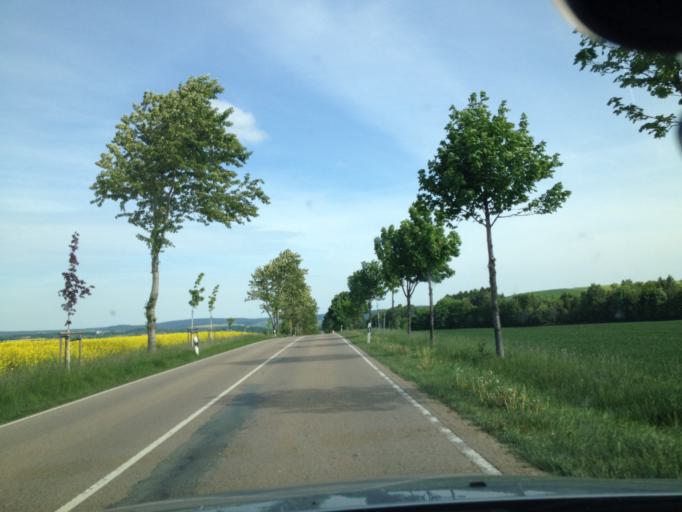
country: DE
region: Saxony
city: Annaberg-Buchholz
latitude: 50.5536
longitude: 13.0169
